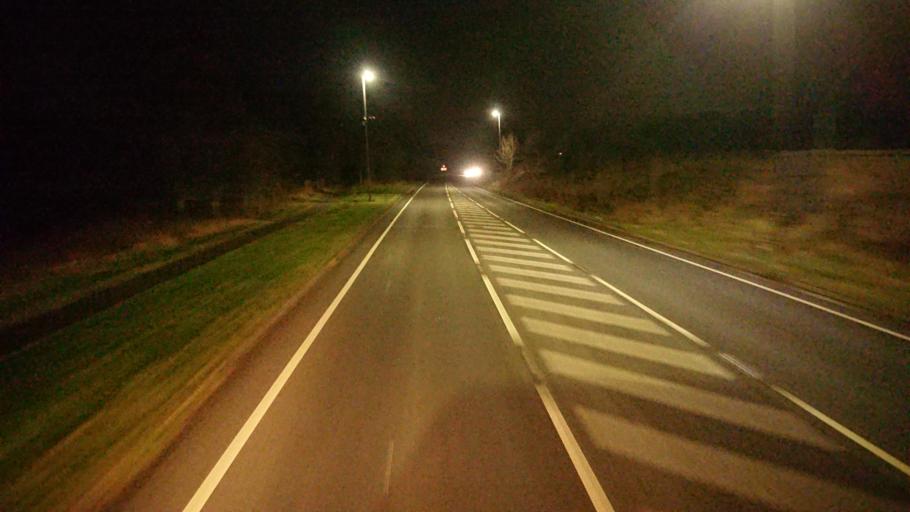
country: GB
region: England
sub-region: Cumbria
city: Kendal
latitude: 54.3680
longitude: -2.8047
